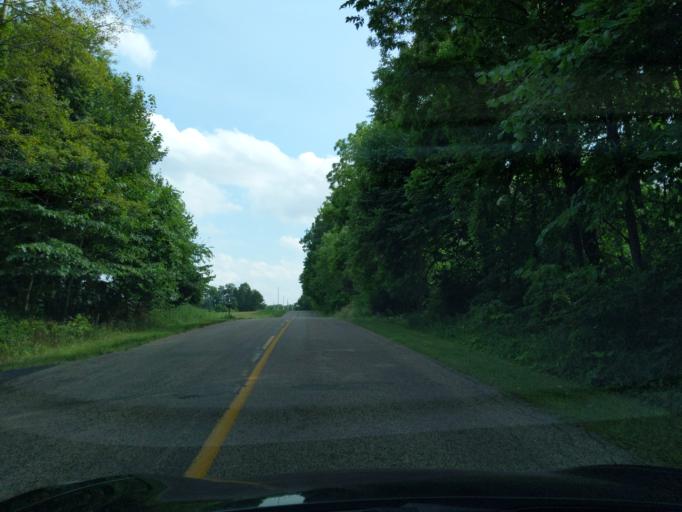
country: US
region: Michigan
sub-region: Eaton County
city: Eaton Rapids
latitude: 42.5314
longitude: -84.6017
